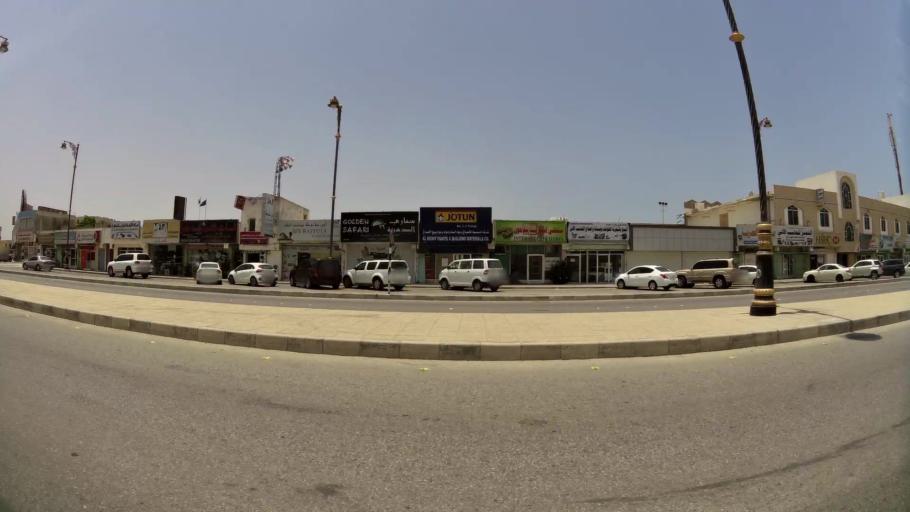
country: OM
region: Zufar
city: Salalah
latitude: 17.0180
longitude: 54.1107
